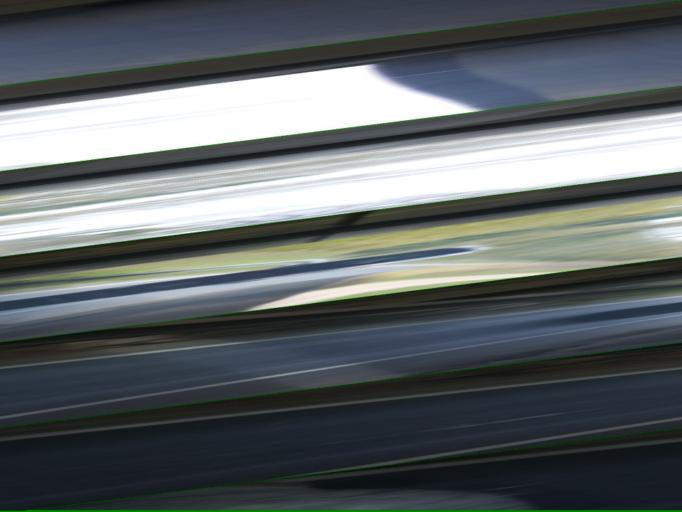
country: FR
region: Ile-de-France
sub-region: Departement des Yvelines
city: Houdan
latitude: 48.7825
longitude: 1.5756
